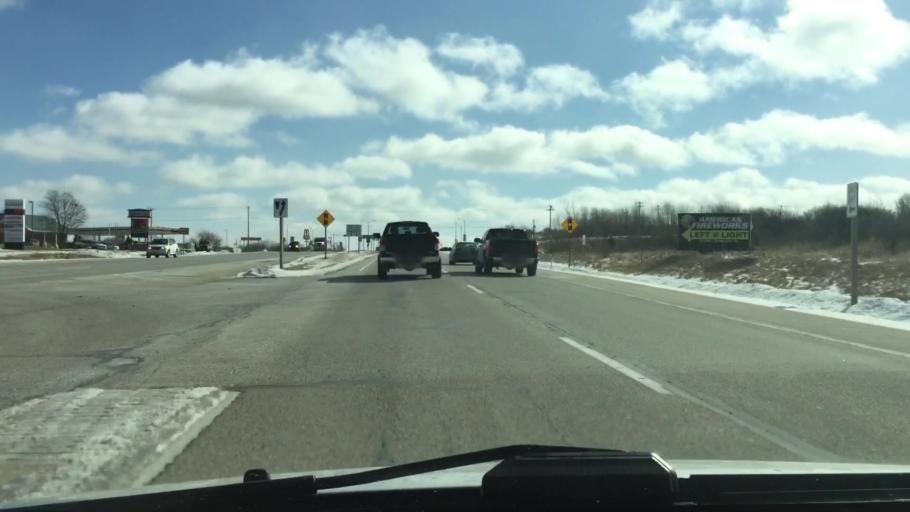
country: US
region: Wisconsin
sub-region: Waukesha County
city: Big Bend
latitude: 42.9161
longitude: -88.2218
